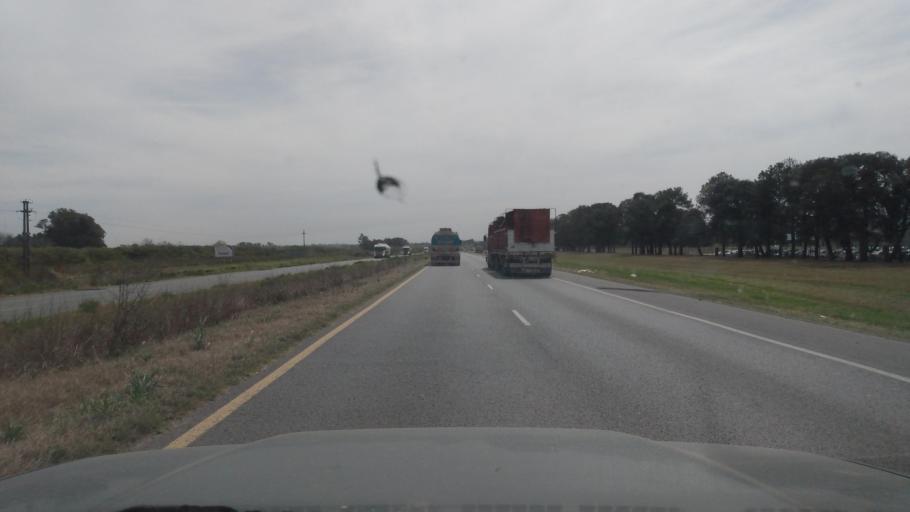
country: AR
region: Buenos Aires
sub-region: Partido de Lujan
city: Lujan
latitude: -34.5362
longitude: -59.0371
